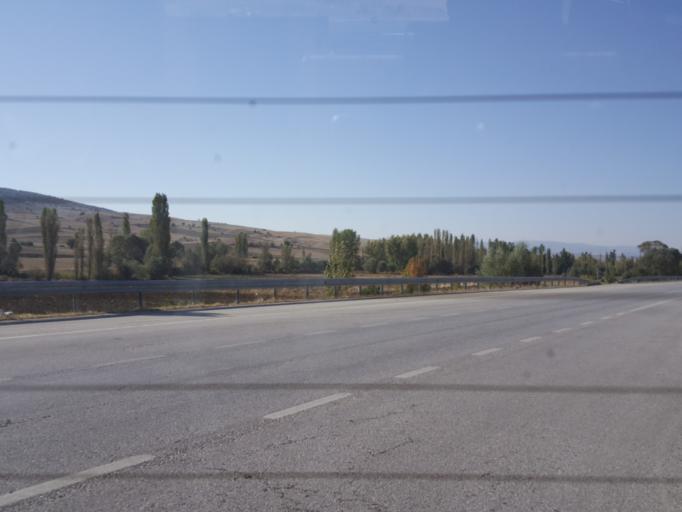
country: TR
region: Corum
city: Bogazkale
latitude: 40.2435
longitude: 34.5919
